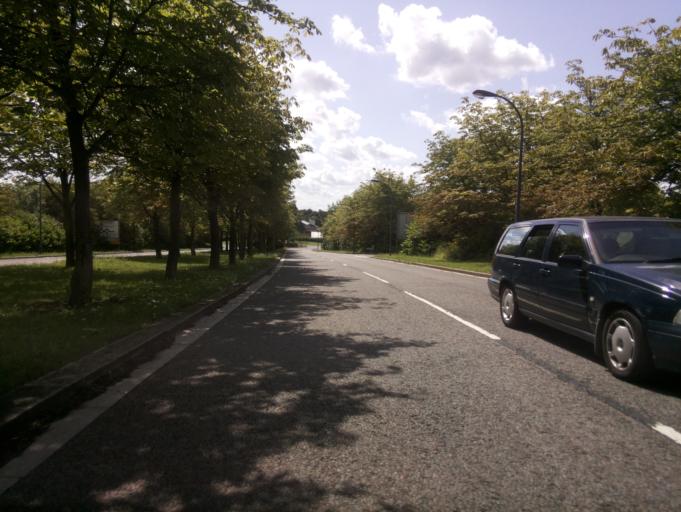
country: GB
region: England
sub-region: Milton Keynes
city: Milton Keynes
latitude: 52.0521
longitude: -0.7390
